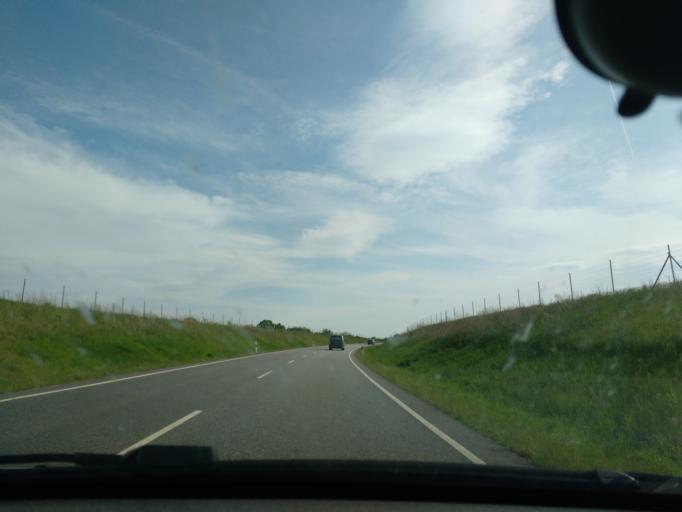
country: DE
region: Schleswig-Holstein
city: Gross Sarau
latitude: 53.7684
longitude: 10.7193
